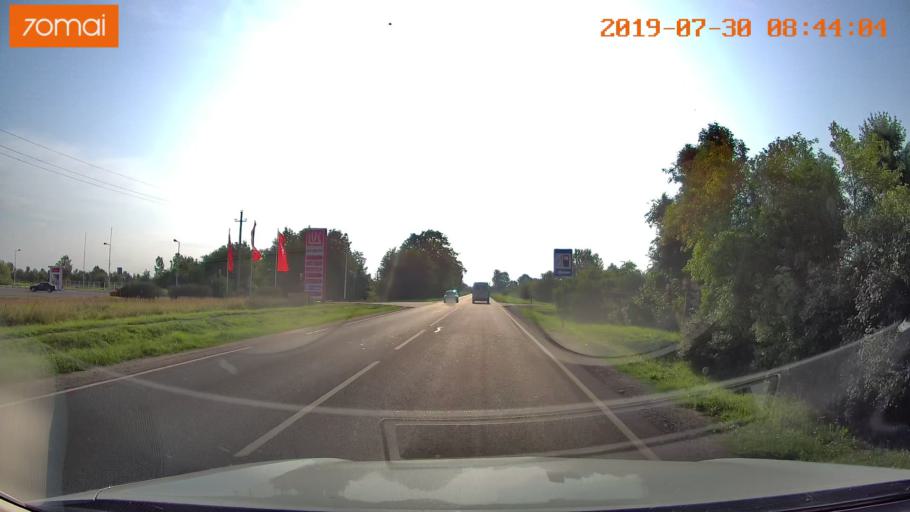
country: RU
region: Kaliningrad
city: Chernyakhovsk
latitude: 54.6266
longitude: 21.8517
